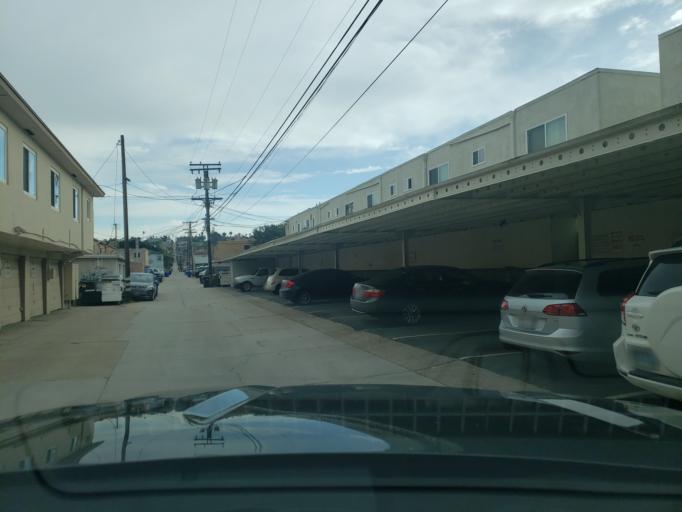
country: US
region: California
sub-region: San Diego County
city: Coronado
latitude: 32.7447
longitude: -117.2528
